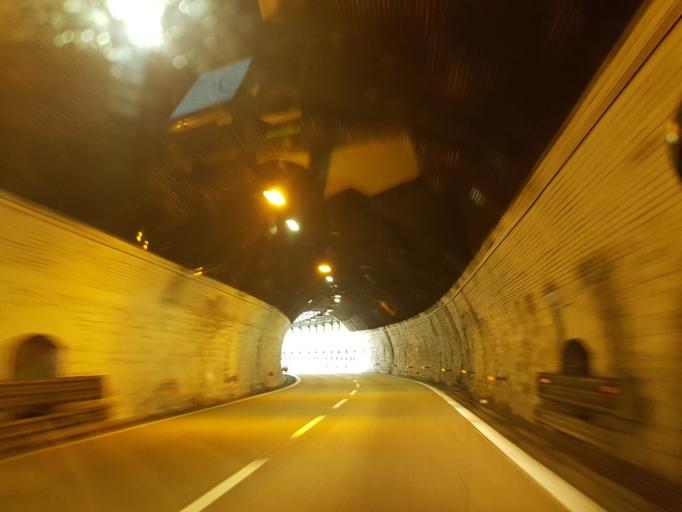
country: IT
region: Liguria
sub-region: Provincia di Genova
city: Manesseno
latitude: 44.4627
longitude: 8.9026
